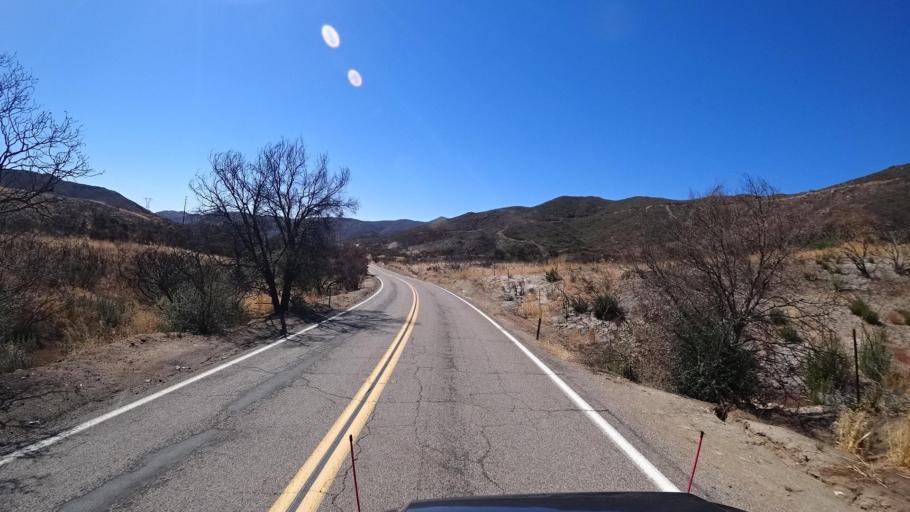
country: US
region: California
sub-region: San Diego County
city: Alpine
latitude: 32.7206
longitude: -116.7049
